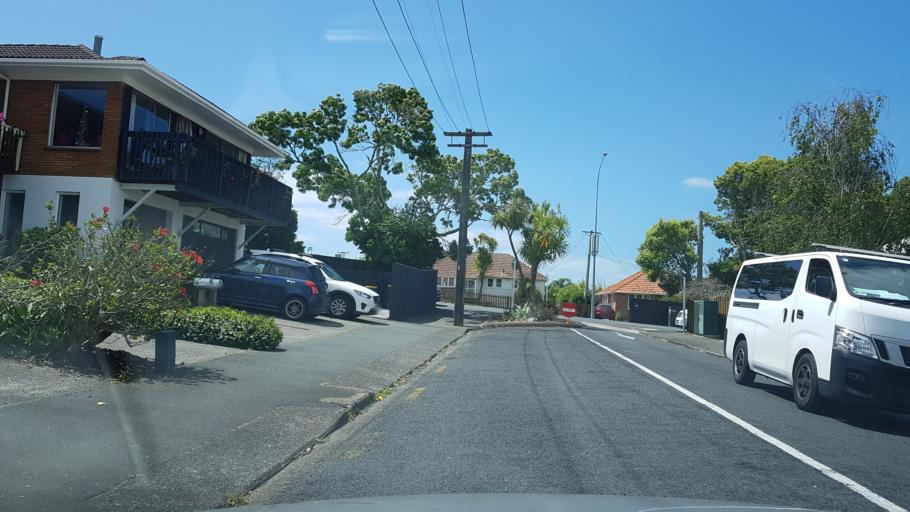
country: NZ
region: Auckland
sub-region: Auckland
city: North Shore
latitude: -36.8111
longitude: 174.7417
